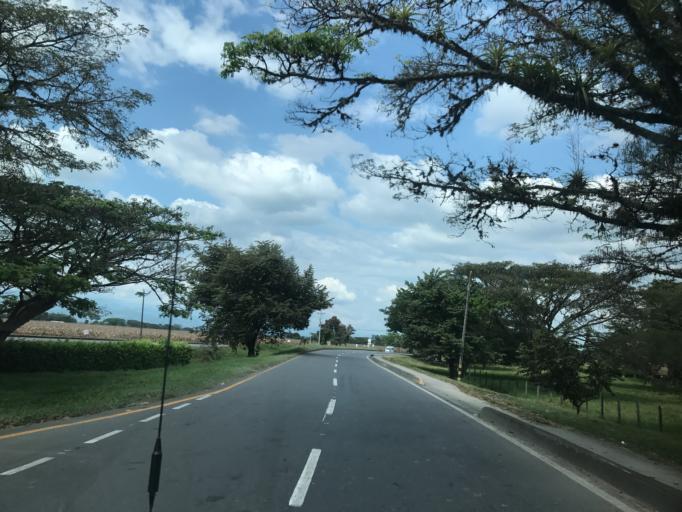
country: CO
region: Valle del Cauca
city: Obando
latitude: 4.5841
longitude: -75.9703
